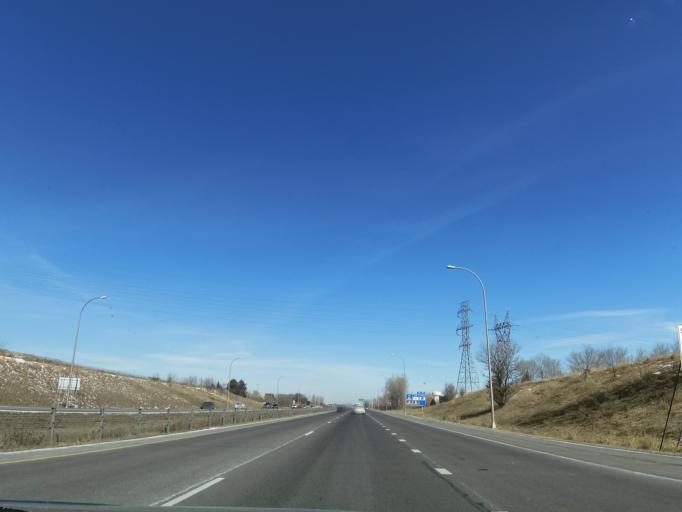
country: US
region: Minnesota
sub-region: Washington County
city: Oakdale
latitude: 44.9539
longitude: -92.9585
